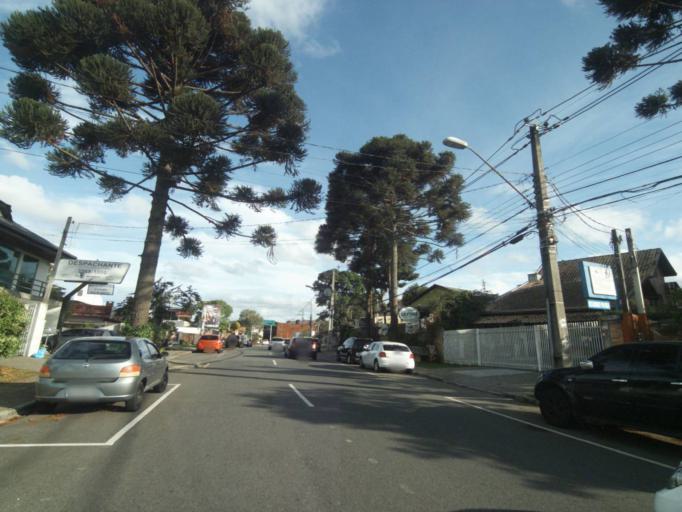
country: BR
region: Parana
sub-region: Curitiba
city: Curitiba
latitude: -25.4381
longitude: -49.3023
